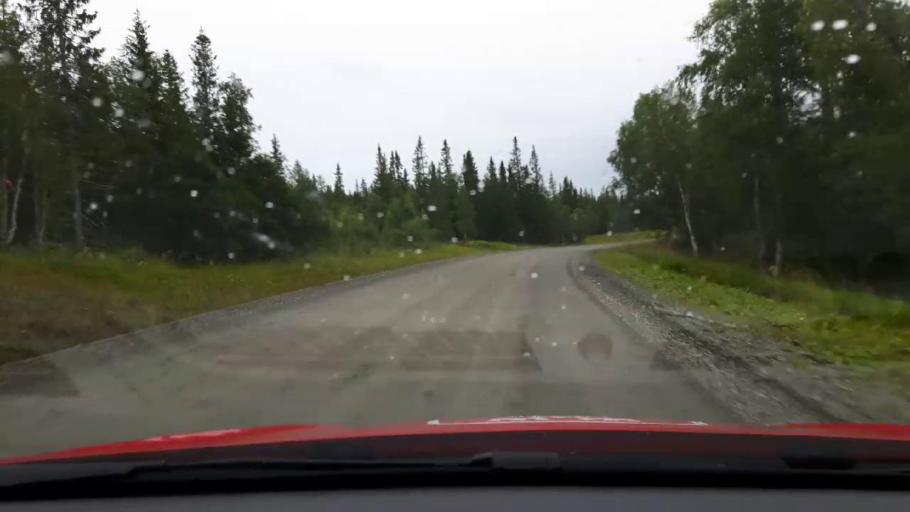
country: NO
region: Nord-Trondelag
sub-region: Meraker
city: Meraker
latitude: 63.5463
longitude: 12.3786
